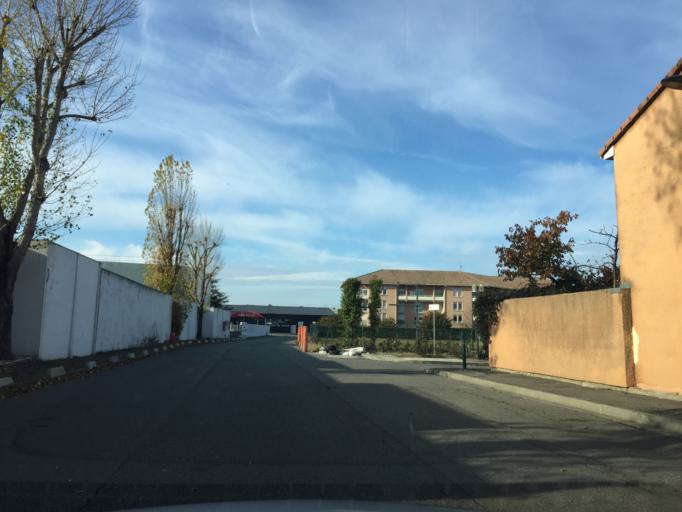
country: FR
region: Midi-Pyrenees
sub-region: Departement de la Haute-Garonne
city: Blagnac
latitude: 43.6108
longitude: 1.3939
